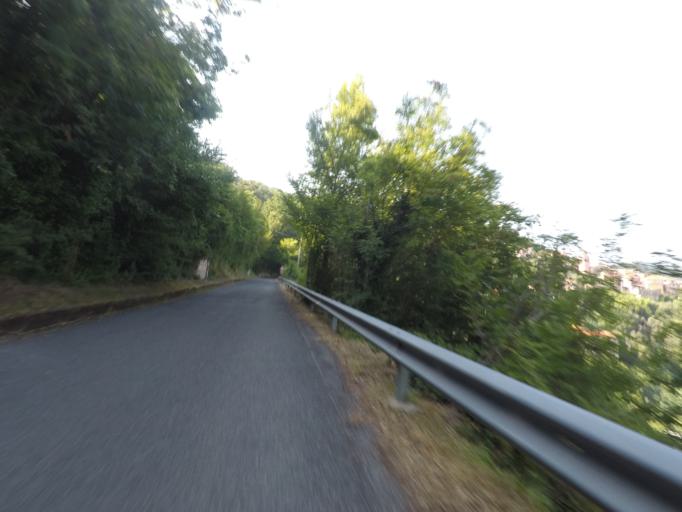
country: IT
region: Tuscany
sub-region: Provincia di Massa-Carrara
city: Carrara
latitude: 44.0728
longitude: 10.0653
